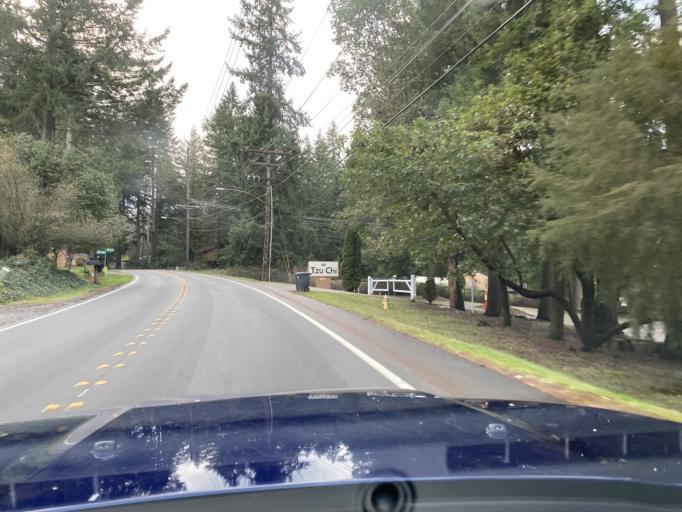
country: US
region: Washington
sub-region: King County
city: Eastgate
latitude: 47.5731
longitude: -122.1286
